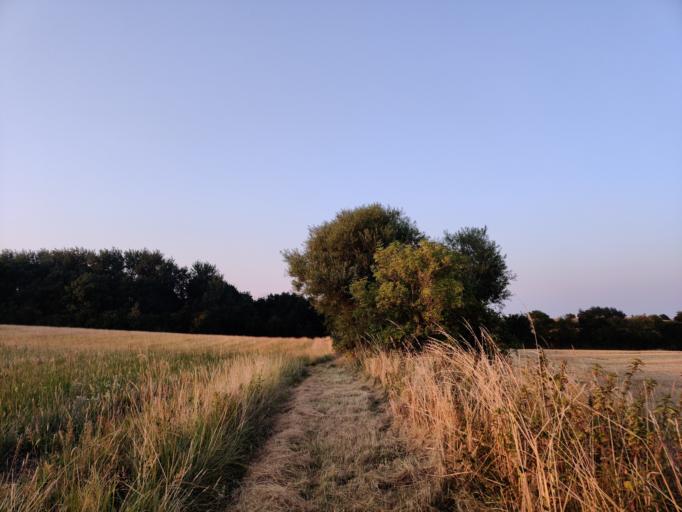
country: DK
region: South Denmark
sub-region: AEro Kommune
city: AEroskobing
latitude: 54.9010
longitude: 10.3137
